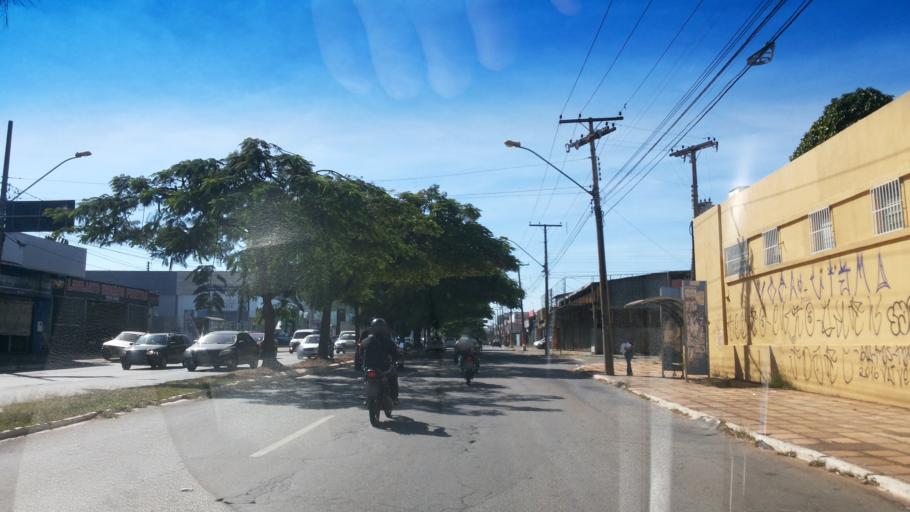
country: BR
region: Goias
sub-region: Goiania
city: Goiania
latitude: -16.6613
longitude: -49.2510
